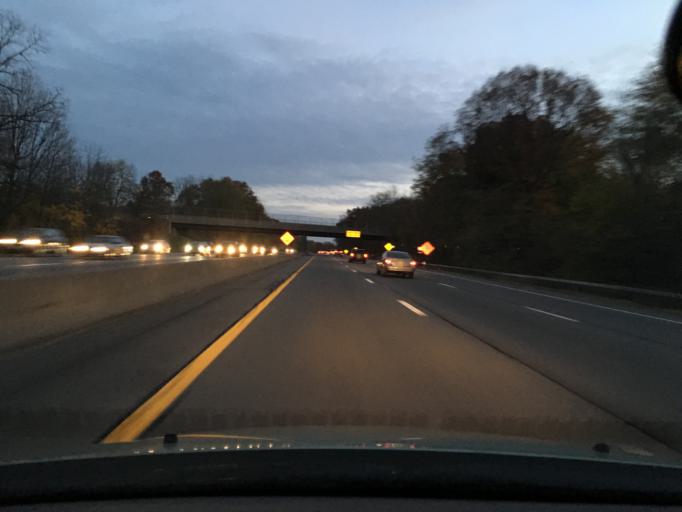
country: US
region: New York
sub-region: Monroe County
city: Pittsford
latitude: 43.1045
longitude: -77.5056
